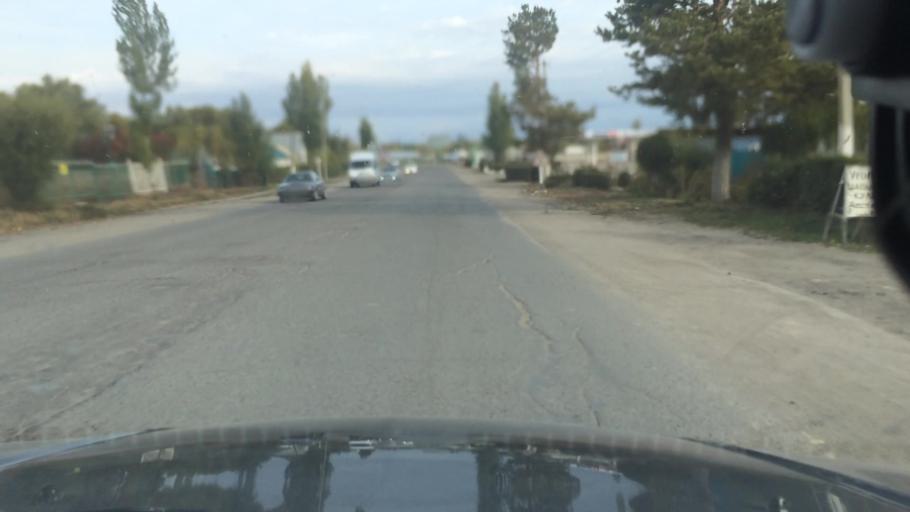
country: KG
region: Ysyk-Koel
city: Karakol
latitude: 42.5210
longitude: 78.3859
